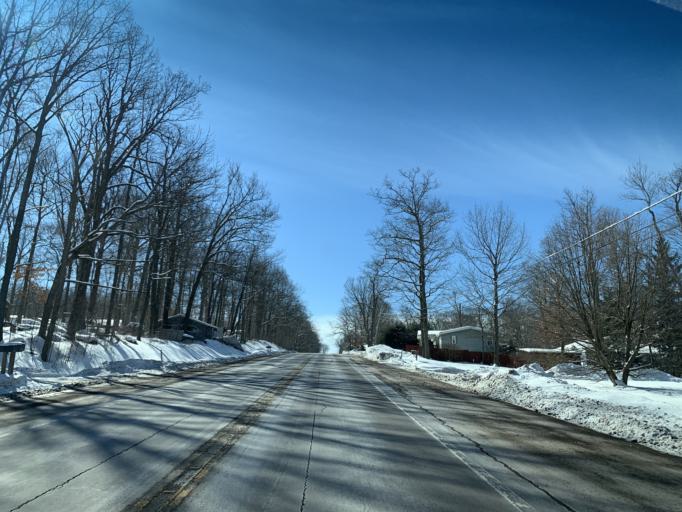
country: US
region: Pennsylvania
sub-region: Somerset County
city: Meyersdale
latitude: 39.7131
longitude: -79.0932
